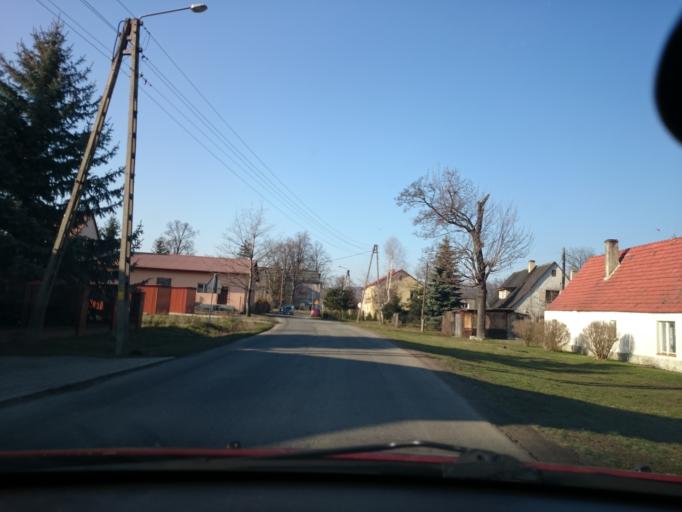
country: PL
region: Lower Silesian Voivodeship
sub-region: Powiat klodzki
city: Klodzko
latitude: 50.3783
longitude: 16.6362
